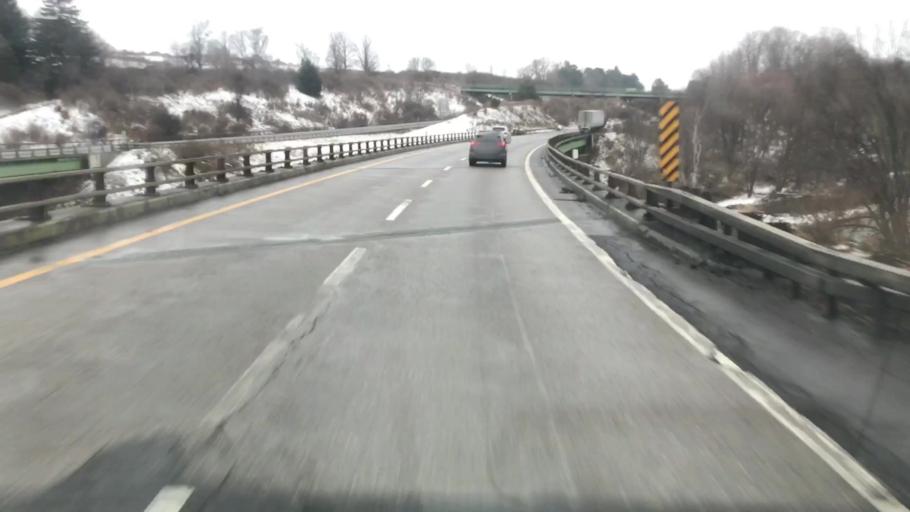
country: US
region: New York
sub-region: Cortland County
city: Cortland
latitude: 42.6068
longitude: -76.1582
